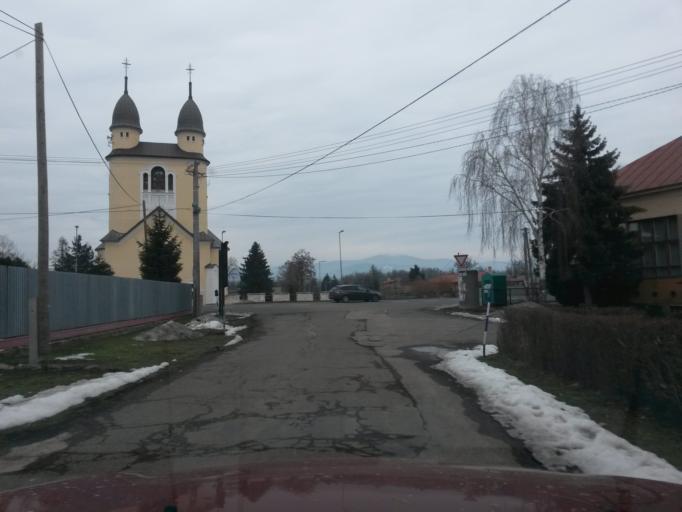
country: SK
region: Kosicky
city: Vinne
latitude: 48.7607
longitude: 21.9936
